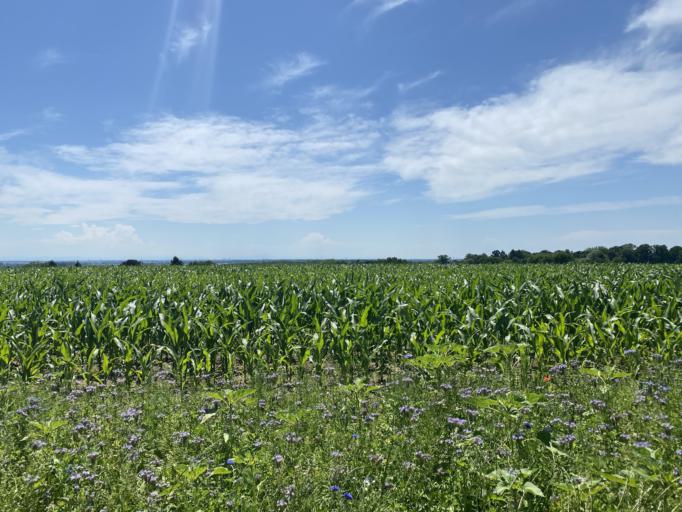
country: DE
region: Bavaria
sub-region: Upper Bavaria
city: Marzling
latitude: 48.4134
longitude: 11.7723
